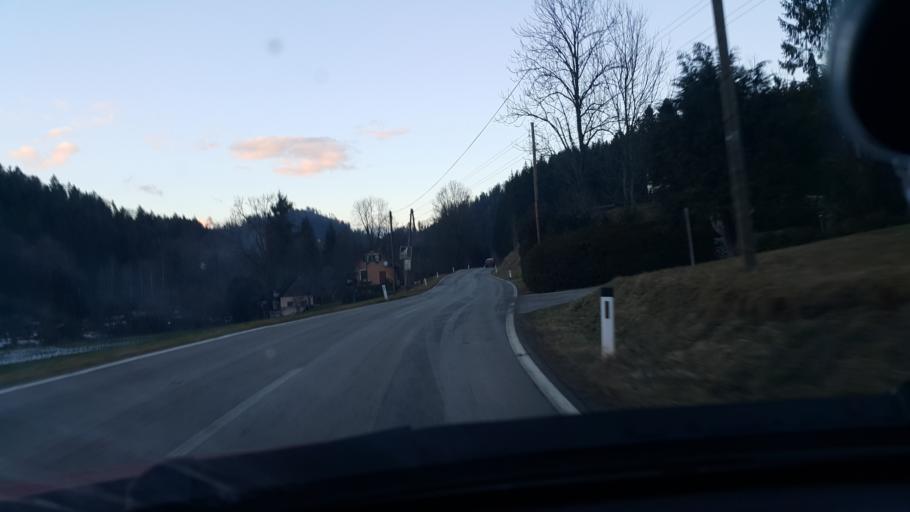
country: AT
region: Styria
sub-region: Politischer Bezirk Graz-Umgebung
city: Stiwoll
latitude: 47.1058
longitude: 15.2167
